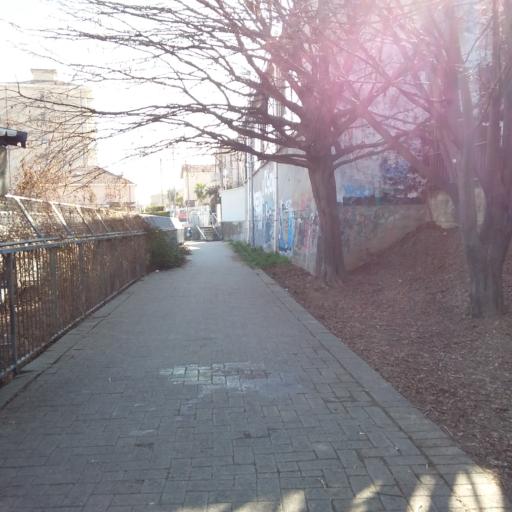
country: IT
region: Piedmont
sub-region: Provincia di Torino
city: Rivoli
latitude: 45.0732
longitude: 7.5364
